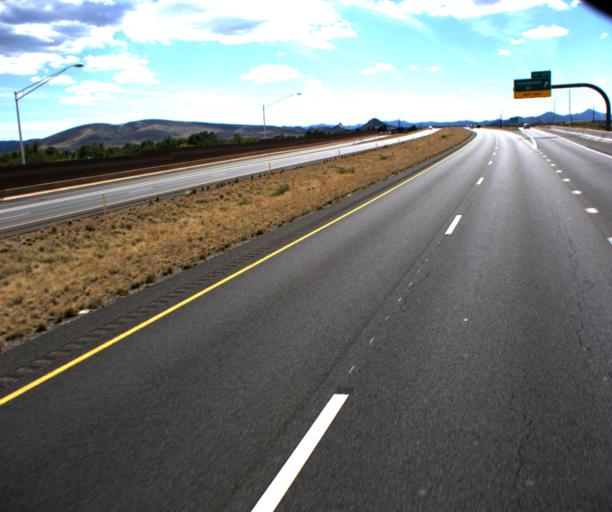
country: US
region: Arizona
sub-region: Yavapai County
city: Prescott Valley
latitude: 34.6386
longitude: -112.3270
